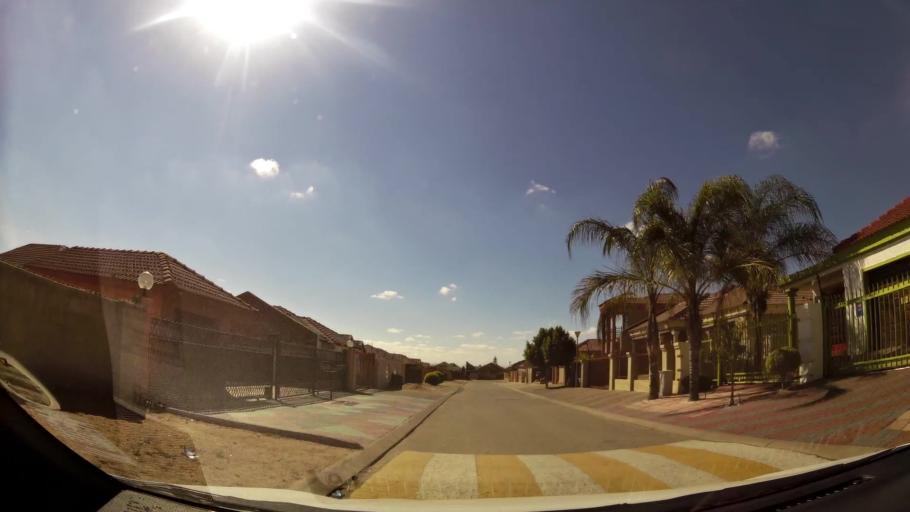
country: ZA
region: Limpopo
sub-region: Capricorn District Municipality
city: Polokwane
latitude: -23.8760
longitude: 29.4134
